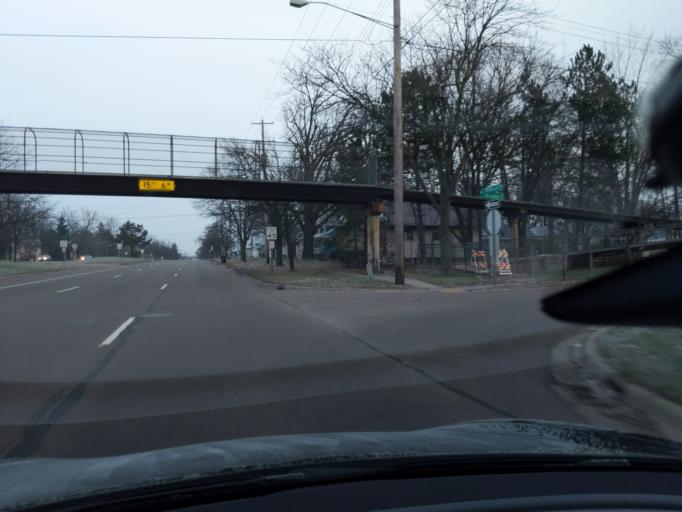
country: US
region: Michigan
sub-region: Ingham County
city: Lansing
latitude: 42.7079
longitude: -84.5674
